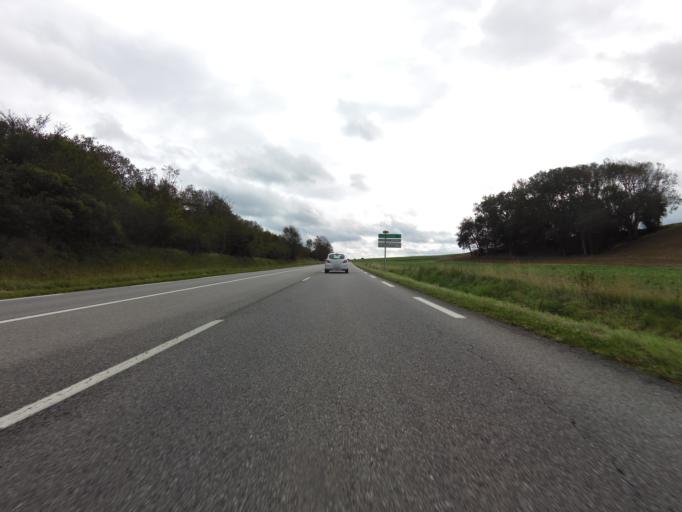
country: FR
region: Haute-Normandie
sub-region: Departement de la Seine-Maritime
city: Criel-sur-Mer
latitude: 50.0218
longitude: 1.3479
